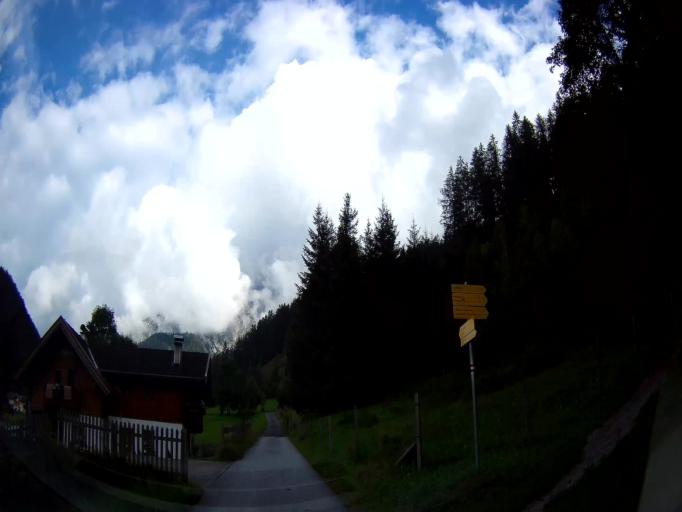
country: AT
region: Salzburg
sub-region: Politischer Bezirk Zell am See
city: Leogang
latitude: 47.4477
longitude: 12.7701
